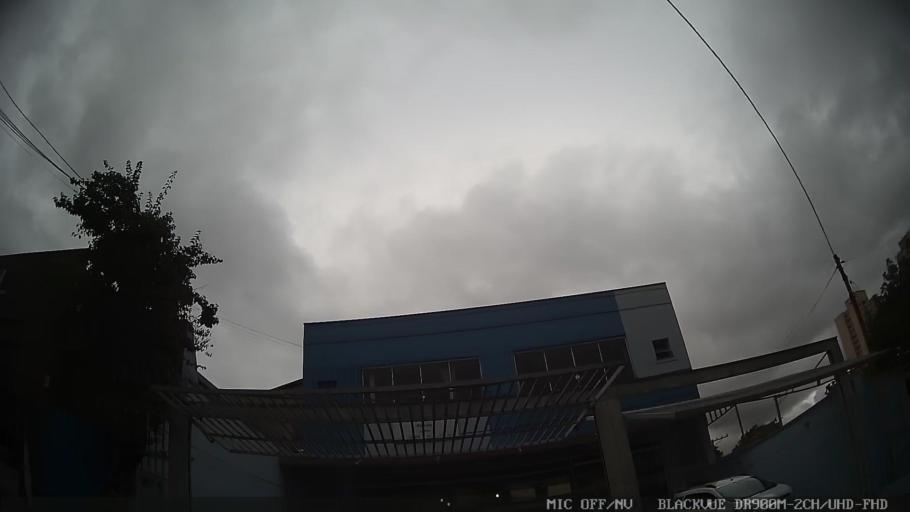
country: BR
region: Sao Paulo
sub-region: Osasco
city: Osasco
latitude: -23.4859
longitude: -46.7219
